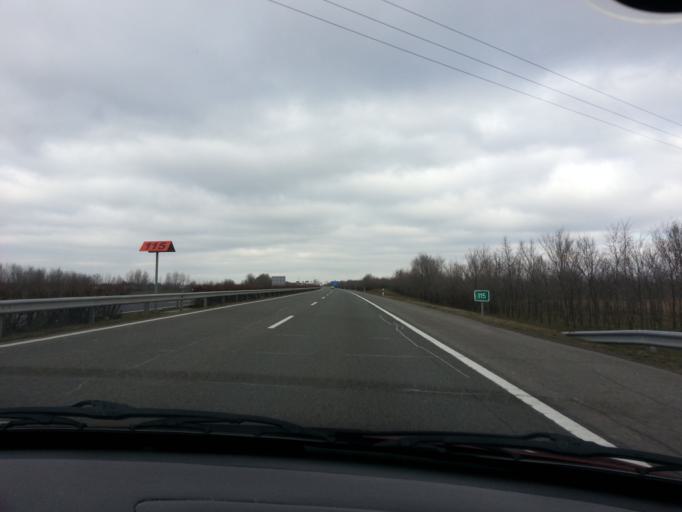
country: HU
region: Bacs-Kiskun
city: Kiskunfelegyhaza
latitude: 46.6661
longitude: 19.8302
